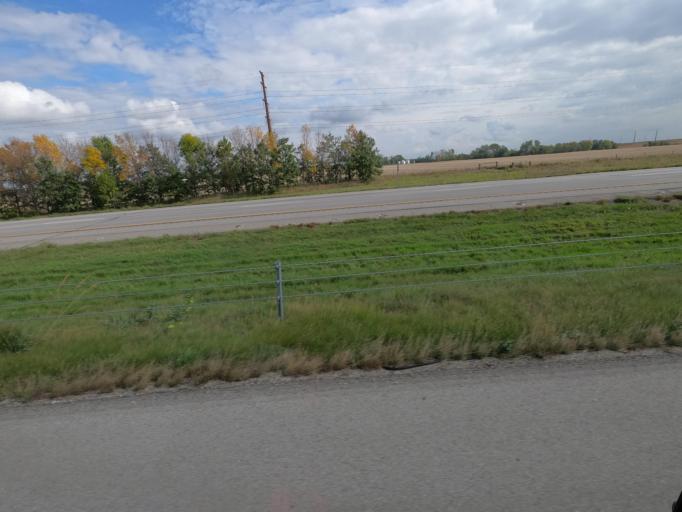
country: US
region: Iowa
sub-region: Story County
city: Huxley
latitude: 41.8829
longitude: -93.5696
